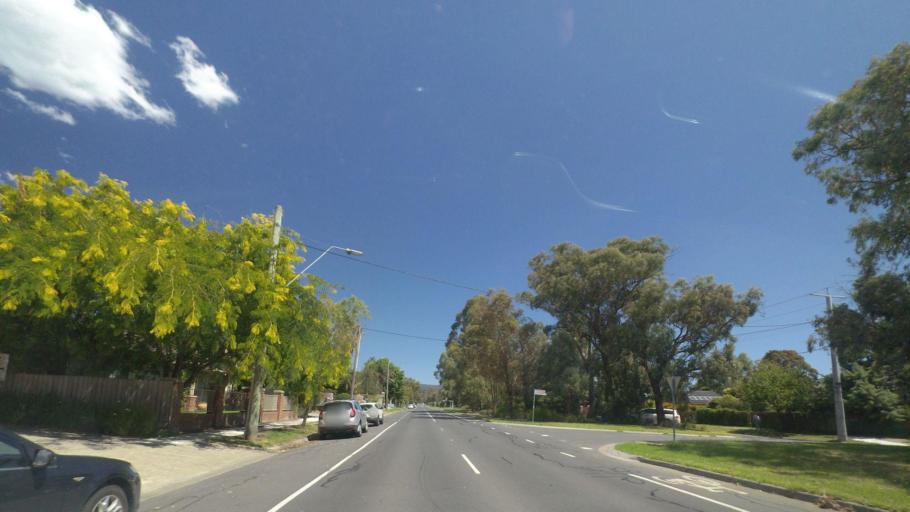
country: AU
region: Victoria
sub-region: Yarra Ranges
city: Kilsyth
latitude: -37.8100
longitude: 145.3158
